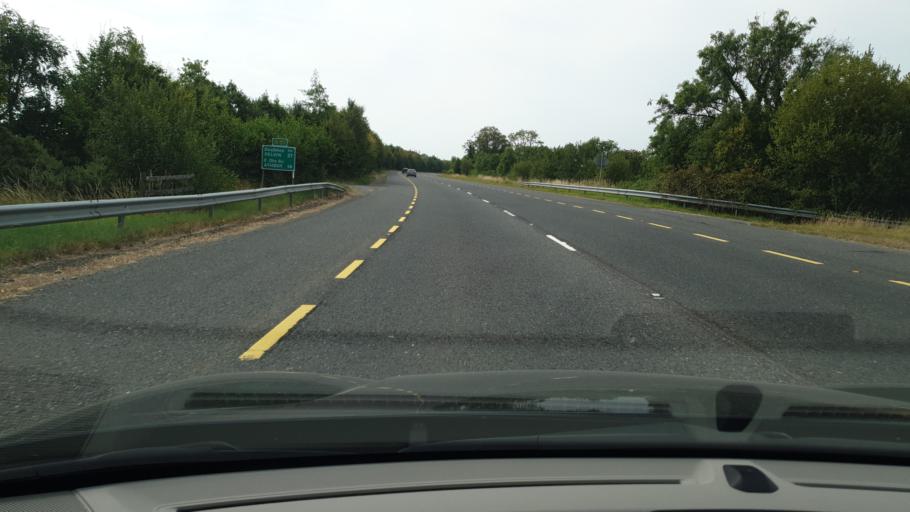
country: IE
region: Leinster
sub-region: An Mhi
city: Navan
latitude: 53.6367
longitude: -6.7437
